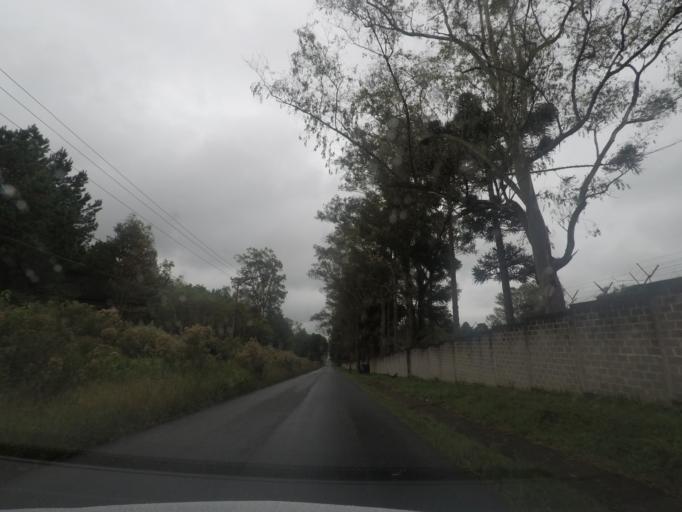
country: BR
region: Parana
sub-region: Quatro Barras
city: Quatro Barras
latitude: -25.3890
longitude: -49.1449
